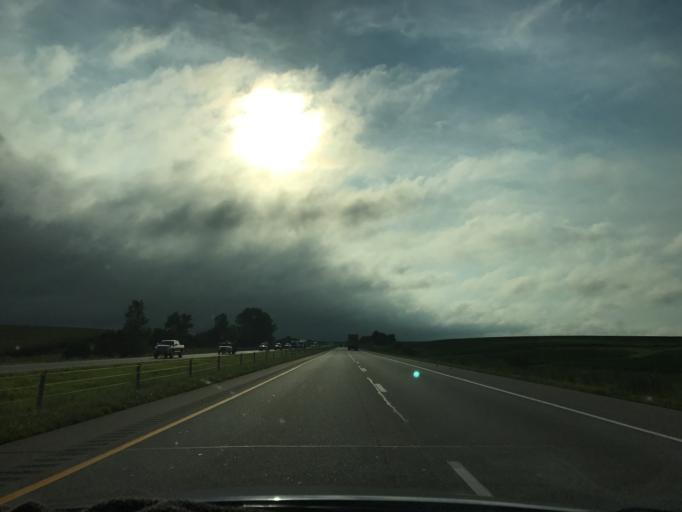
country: US
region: Iowa
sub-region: Muscatine County
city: West Liberty
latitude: 41.6609
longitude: -91.2233
